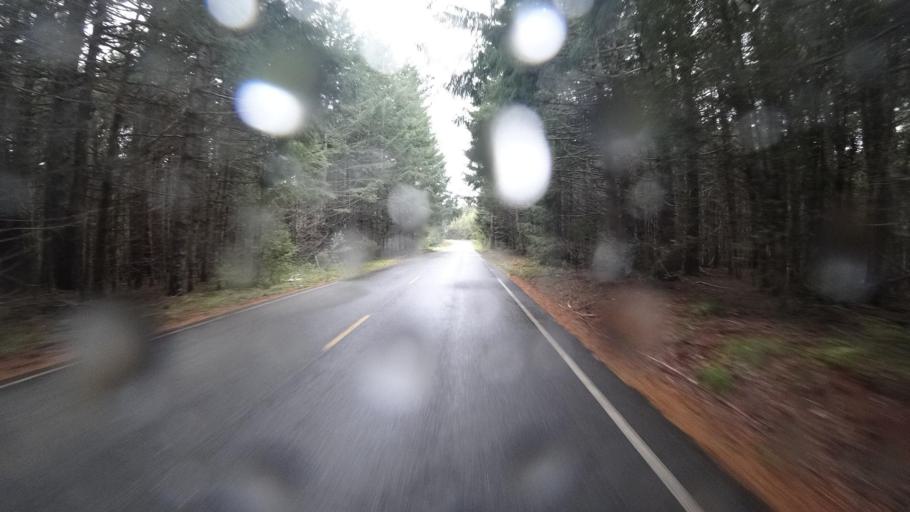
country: US
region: California
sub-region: Humboldt County
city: Willow Creek
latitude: 41.1933
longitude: -123.8121
